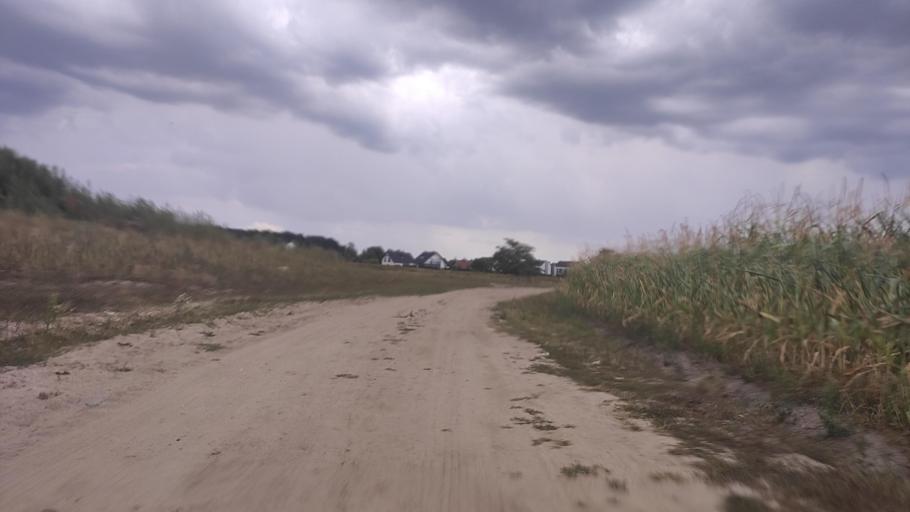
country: PL
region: Greater Poland Voivodeship
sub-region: Powiat poznanski
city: Swarzedz
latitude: 52.3936
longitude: 17.1233
